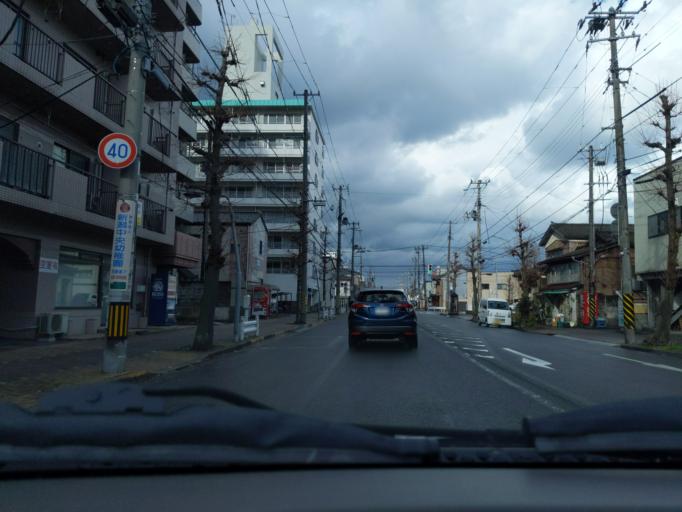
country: JP
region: Niigata
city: Niigata-shi
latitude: 37.9277
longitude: 139.0471
